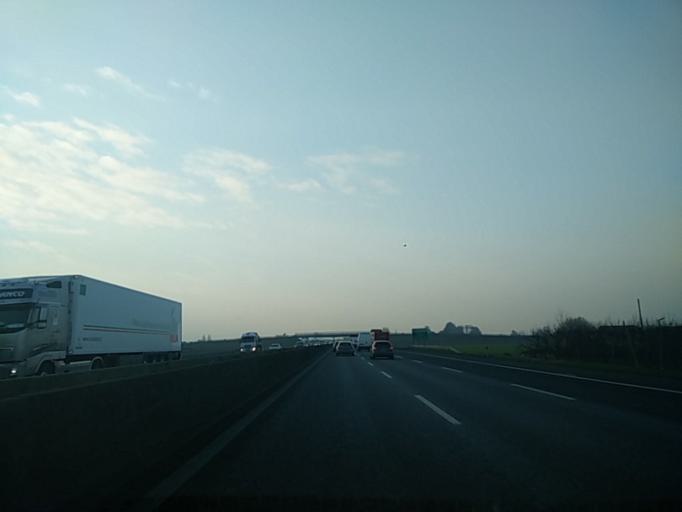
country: IT
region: Emilia-Romagna
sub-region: Provincia di Bologna
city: Bubano
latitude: 44.3716
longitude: 11.7677
